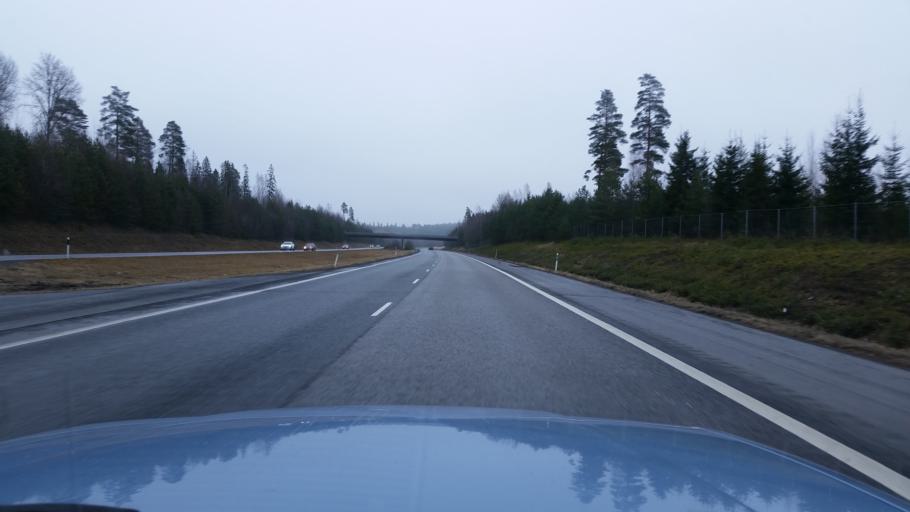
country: FI
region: Haeme
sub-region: Haemeenlinna
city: Parola
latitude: 61.0704
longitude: 24.2979
